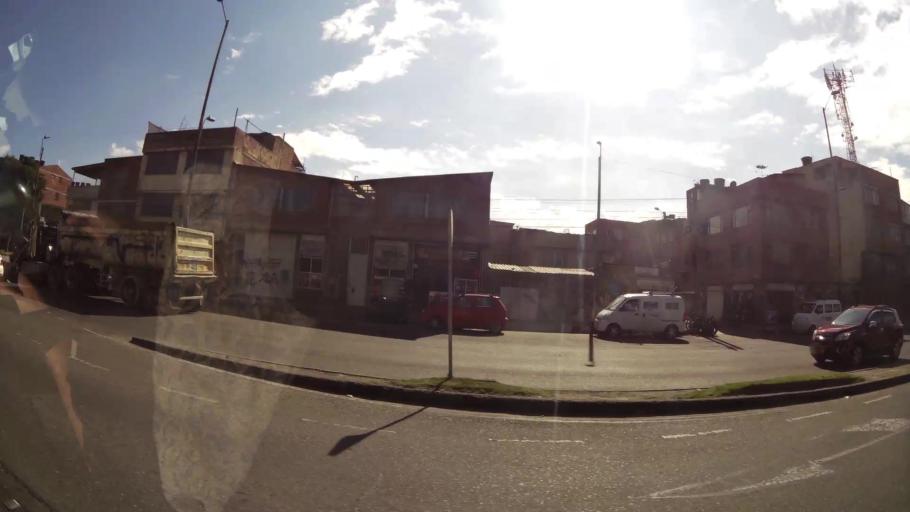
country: CO
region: Bogota D.C.
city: Bogota
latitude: 4.5789
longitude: -74.1419
